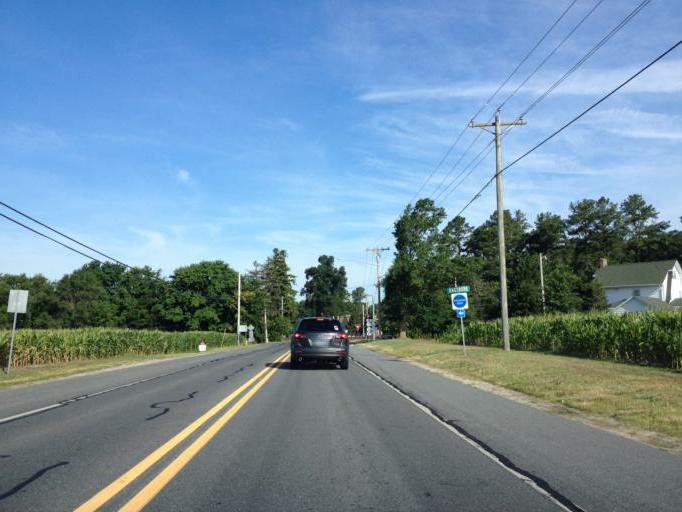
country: US
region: Delaware
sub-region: Sussex County
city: Millsboro
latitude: 38.5474
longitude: -75.2363
